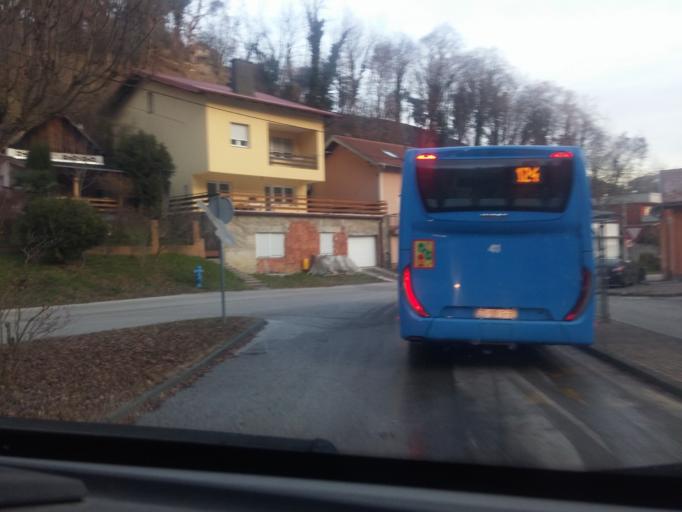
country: HR
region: Grad Zagreb
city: Stenjevec
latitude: 45.8331
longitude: 15.8696
